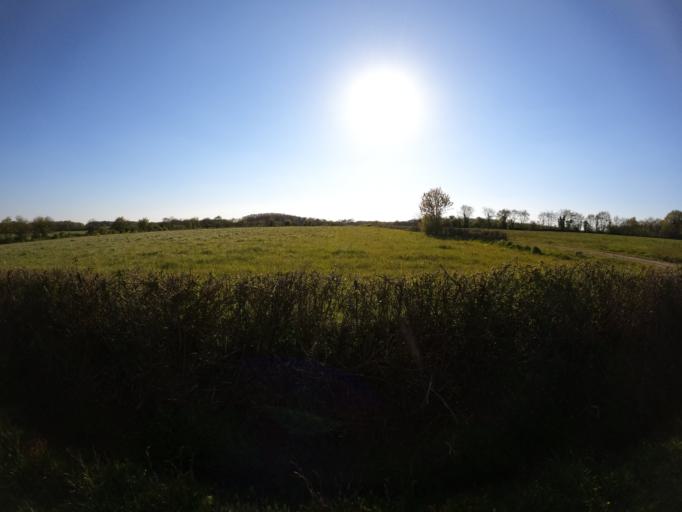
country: FR
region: Pays de la Loire
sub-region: Departement de la Vendee
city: Les Brouzils
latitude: 46.8946
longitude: -1.3682
